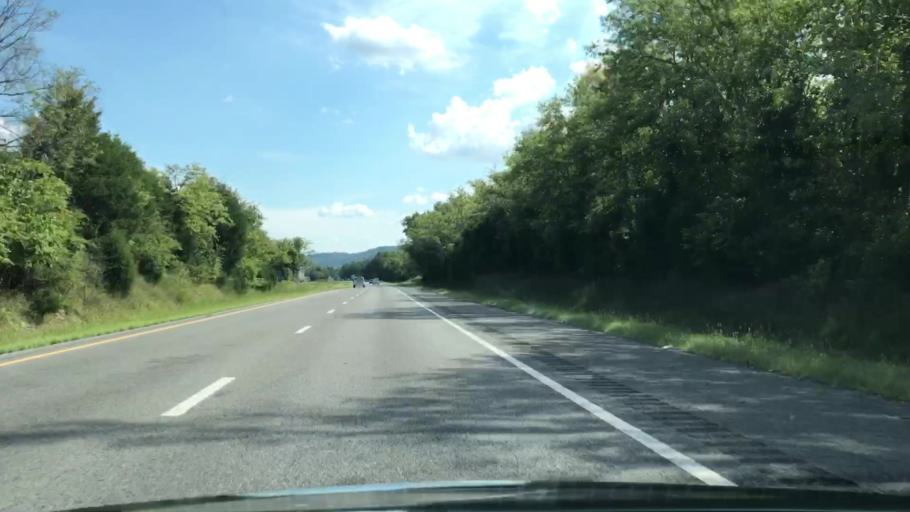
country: US
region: Tennessee
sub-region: Marshall County
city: Lewisburg
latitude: 35.4635
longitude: -86.8869
